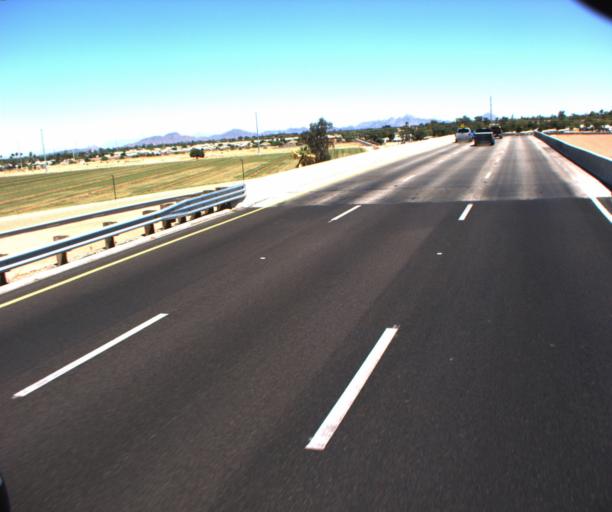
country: US
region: Arizona
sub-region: Maricopa County
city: Peoria
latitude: 33.5635
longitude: -112.2166
